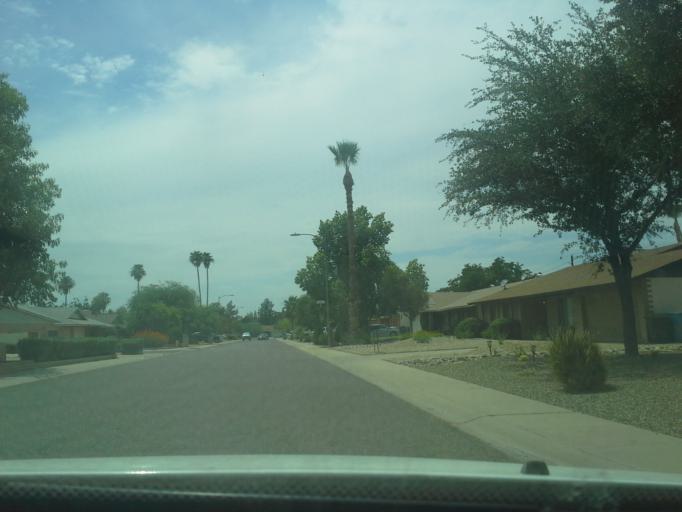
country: US
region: Arizona
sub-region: Maricopa County
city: Paradise Valley
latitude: 33.6111
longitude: -111.9831
